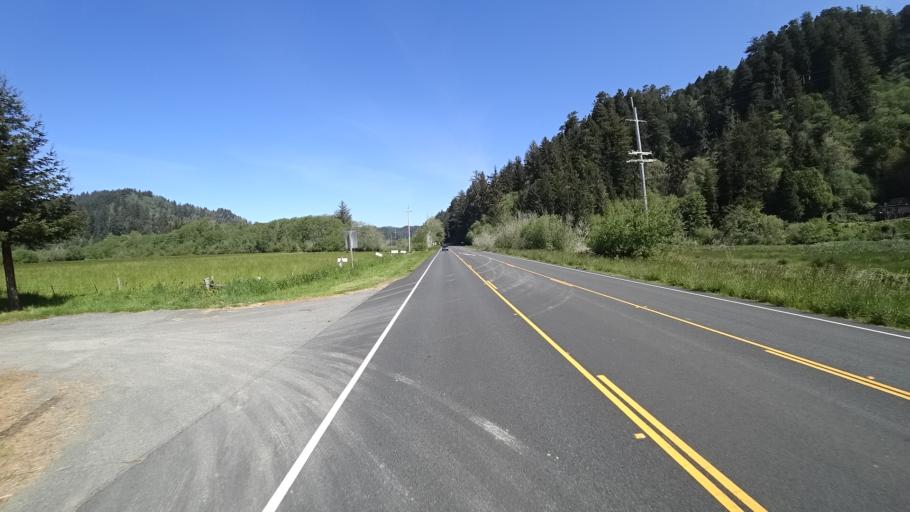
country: US
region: California
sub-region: Del Norte County
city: Bertsch-Oceanview
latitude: 41.5442
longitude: -124.0514
